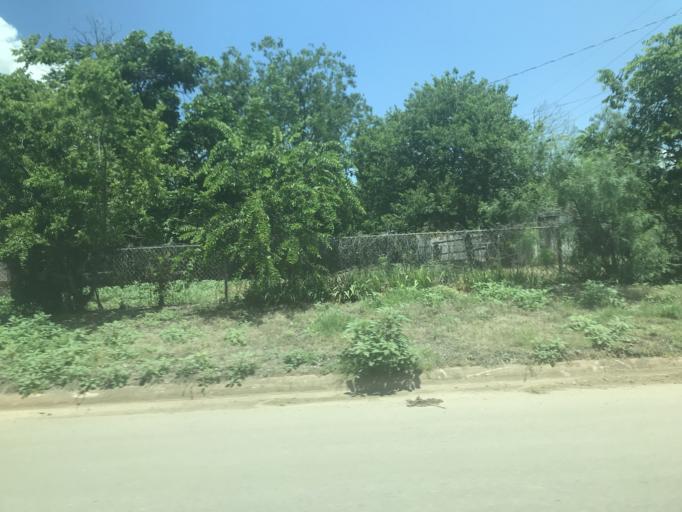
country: US
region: Texas
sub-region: Taylor County
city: Abilene
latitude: 32.4671
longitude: -99.7541
